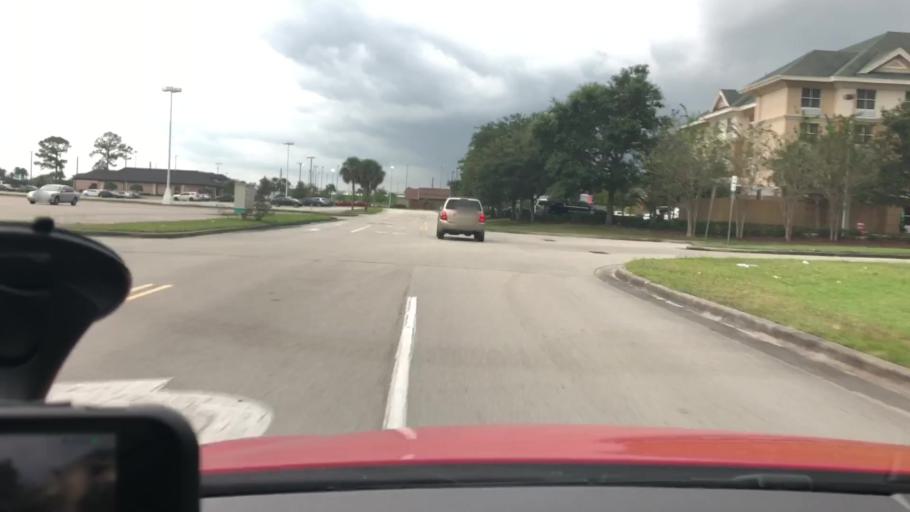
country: US
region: Florida
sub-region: Volusia County
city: Daytona Beach
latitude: 29.1960
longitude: -81.0668
